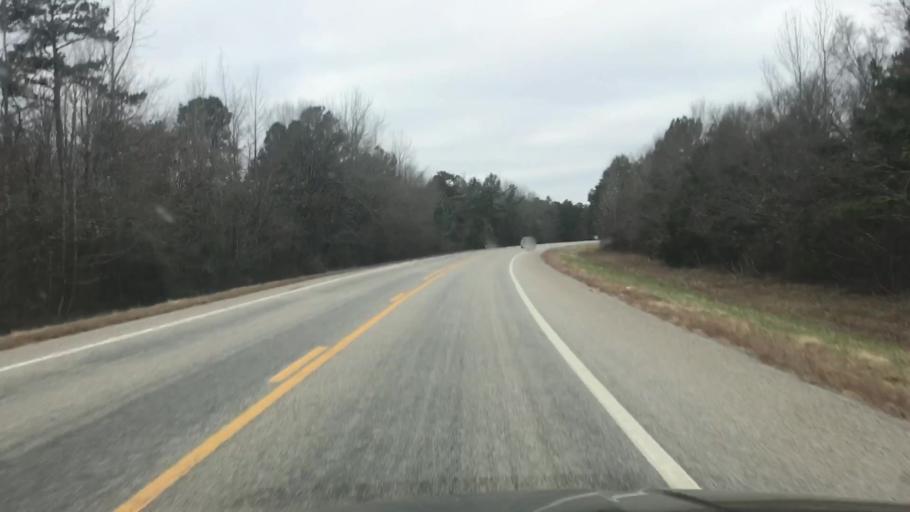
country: US
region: Arkansas
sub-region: Scott County
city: Waldron
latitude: 34.7042
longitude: -93.9269
